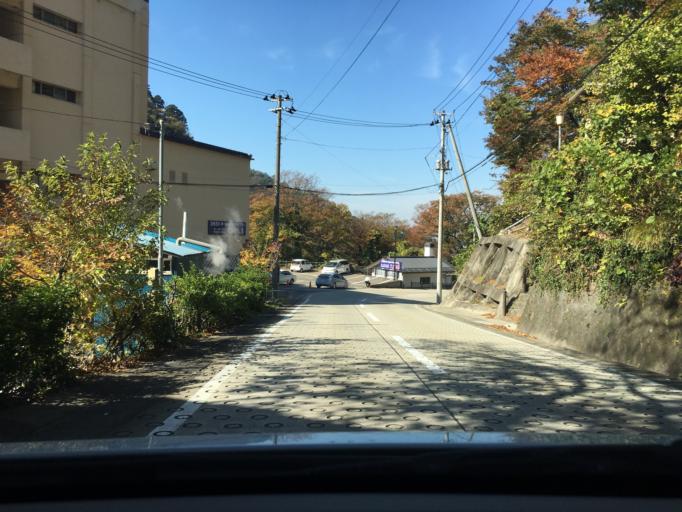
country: JP
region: Fukushima
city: Inawashiro
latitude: 37.4798
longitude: 139.9614
